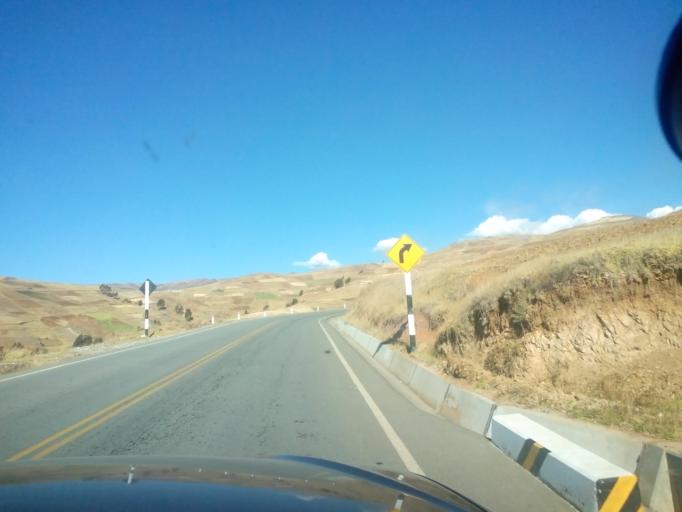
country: PE
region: Apurimac
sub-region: Provincia de Andahuaylas
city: Pacucha
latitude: -13.6540
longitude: -73.2910
